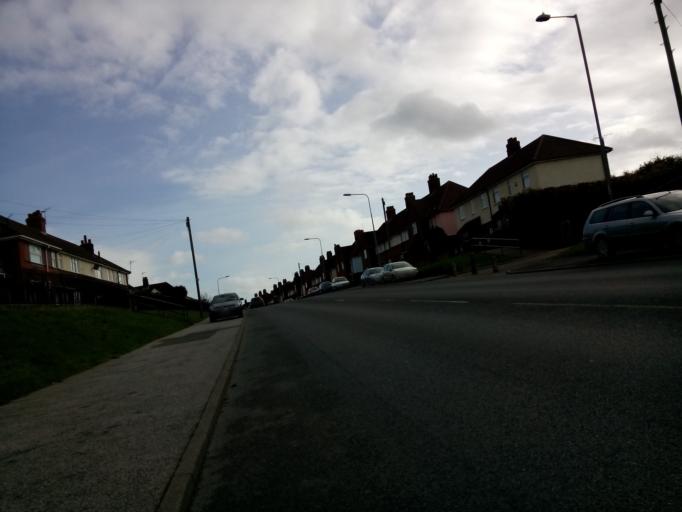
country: GB
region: England
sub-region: Suffolk
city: Ipswich
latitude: 52.0376
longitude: 1.1728
